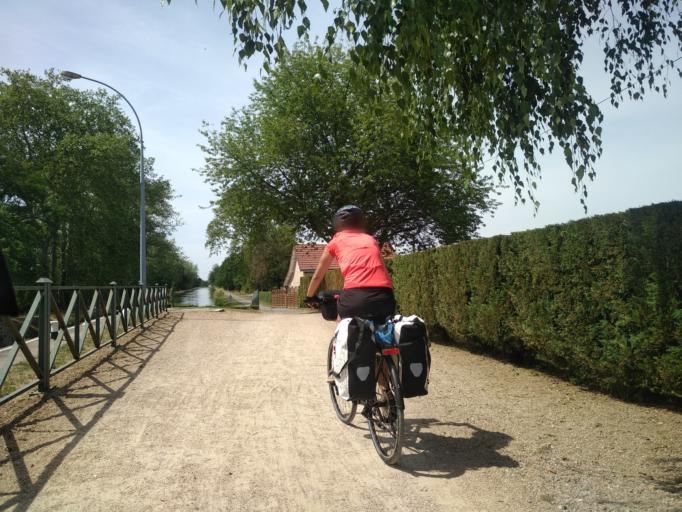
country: FR
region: Auvergne
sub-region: Departement de l'Allier
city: Diou
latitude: 46.4950
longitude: 3.8391
